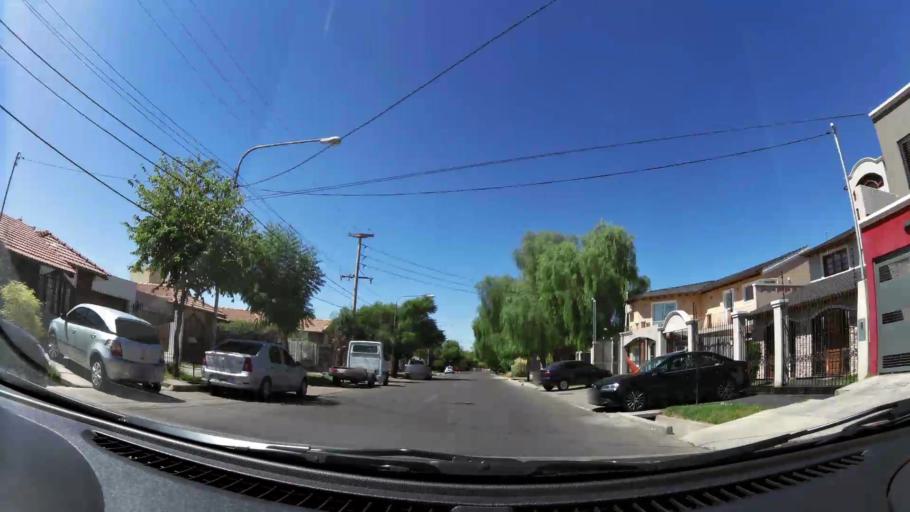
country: AR
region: Mendoza
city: Las Heras
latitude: -32.8527
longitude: -68.8542
